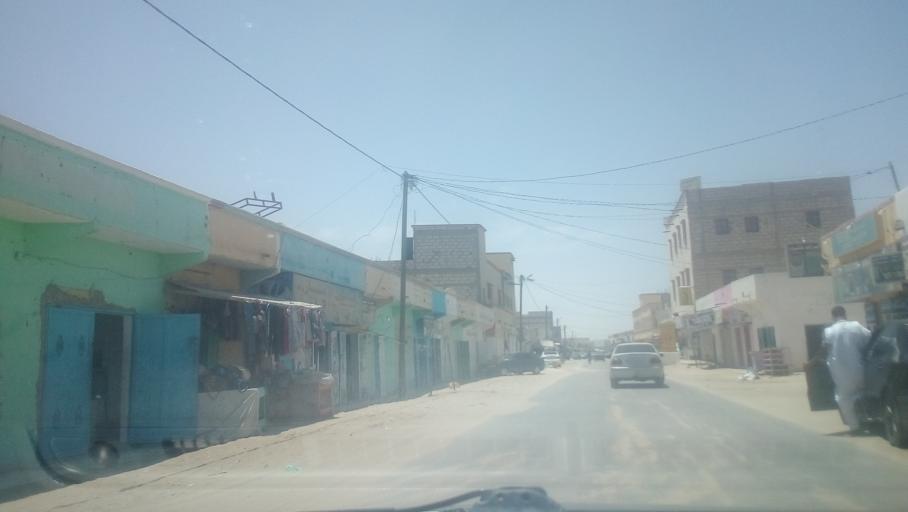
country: MR
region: Nouakchott
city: Nouakchott
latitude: 18.0581
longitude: -15.9611
